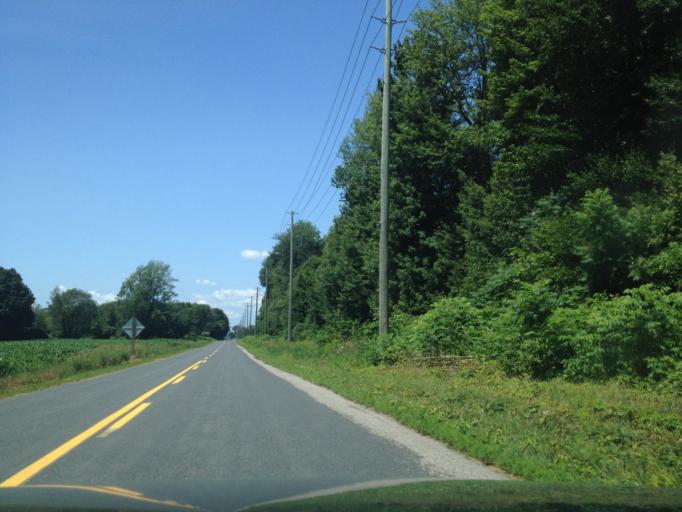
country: CA
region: Ontario
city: Aylmer
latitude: 42.6386
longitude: -80.7228
